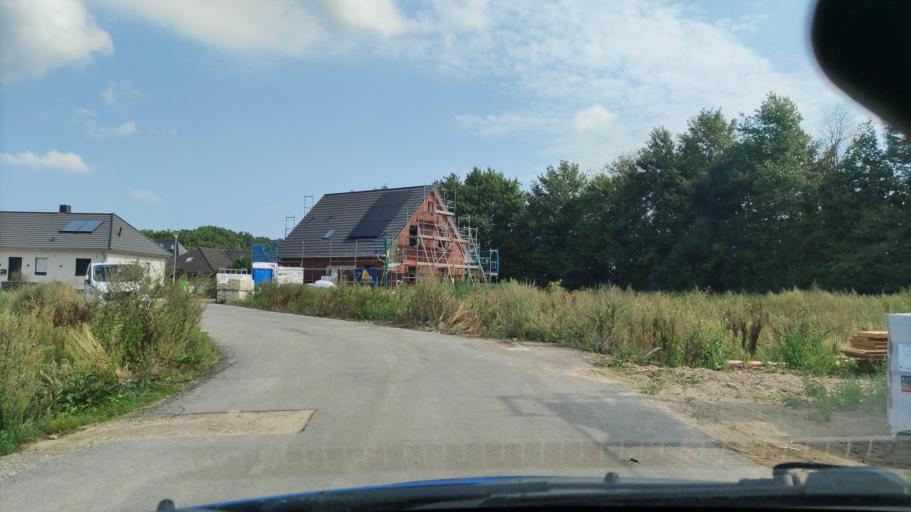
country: DE
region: Lower Saxony
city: Barum
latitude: 53.3431
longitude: 10.4130
